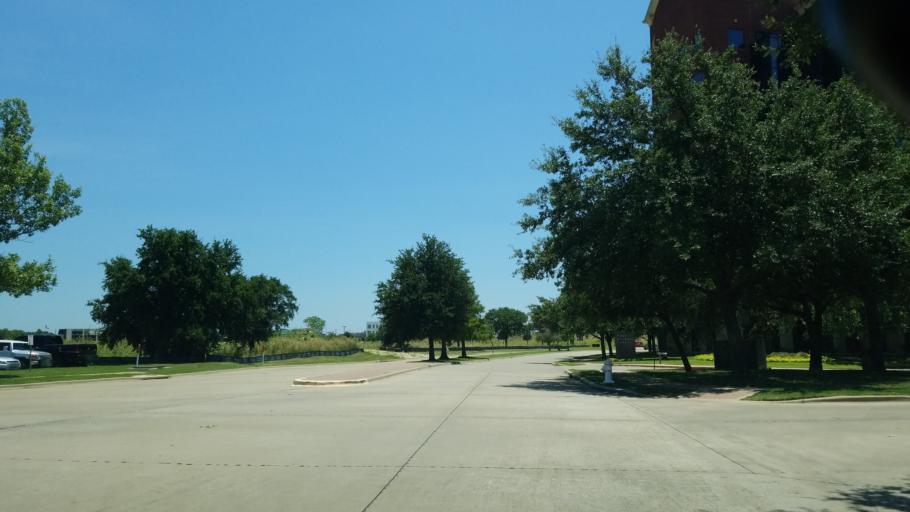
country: US
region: Texas
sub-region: Dallas County
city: Farmers Branch
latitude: 32.9182
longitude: -96.9197
